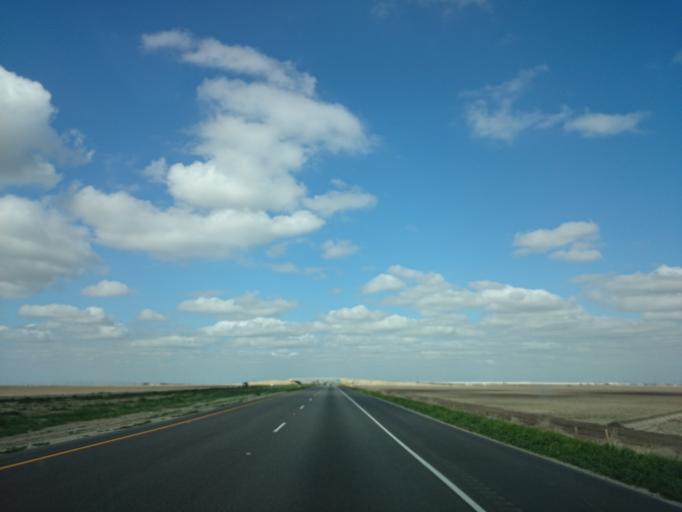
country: US
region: California
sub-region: Kern County
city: Greenfield
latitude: 35.1469
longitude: -119.0941
